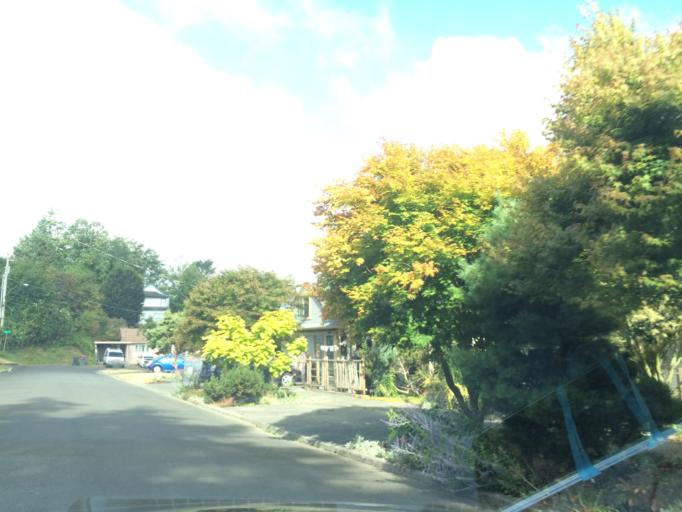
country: US
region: Oregon
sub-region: Clatsop County
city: Astoria
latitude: 46.1827
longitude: -123.8320
